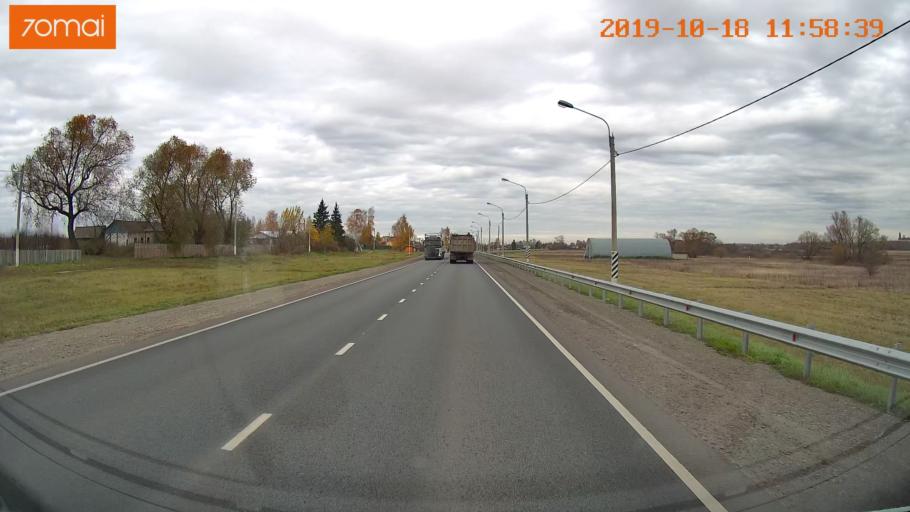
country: RU
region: Rjazan
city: Zakharovo
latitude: 54.2741
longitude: 39.1688
